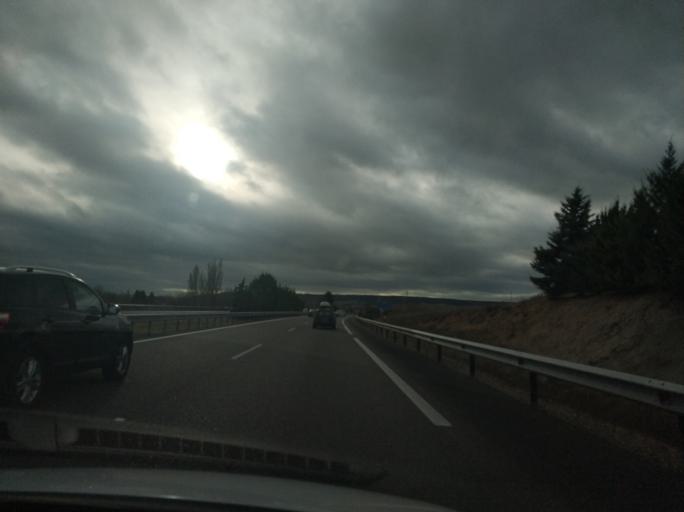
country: ES
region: Castille and Leon
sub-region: Provincia de Palencia
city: Venta de Banos
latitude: 41.9403
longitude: -4.4879
